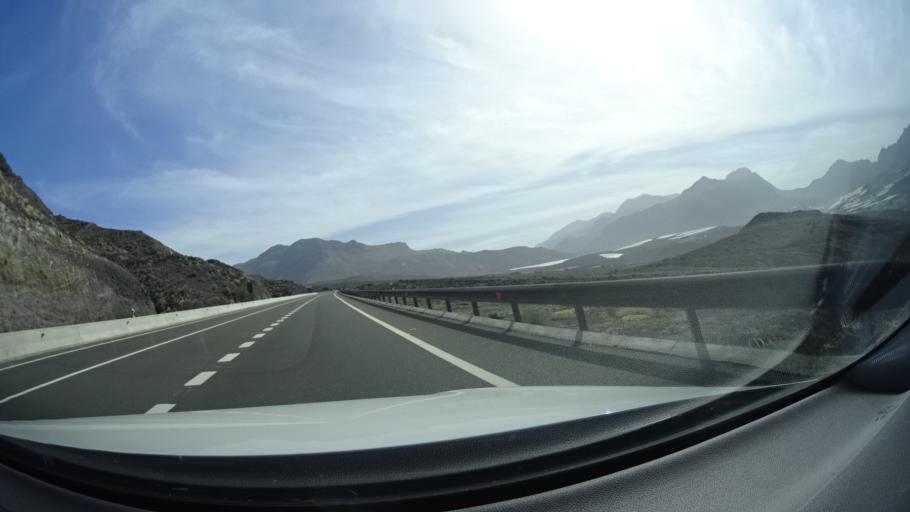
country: ES
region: Canary Islands
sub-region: Provincia de Las Palmas
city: San Nicolas
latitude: 28.0079
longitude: -15.7963
